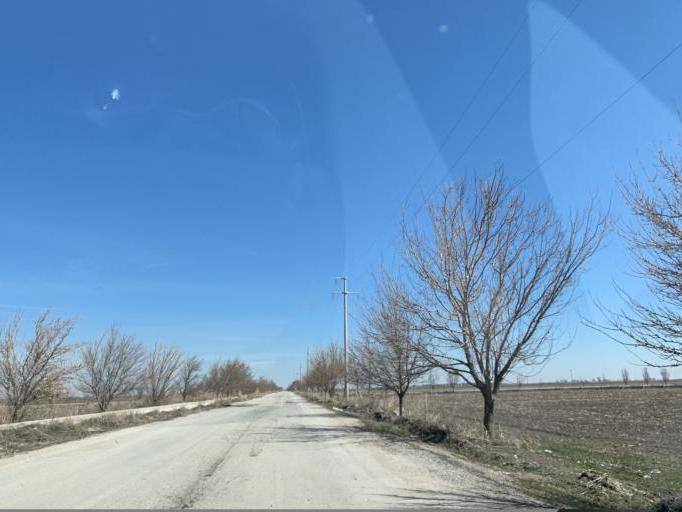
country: TR
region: Konya
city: Catalhoeyuek
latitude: 37.7423
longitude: 32.8031
